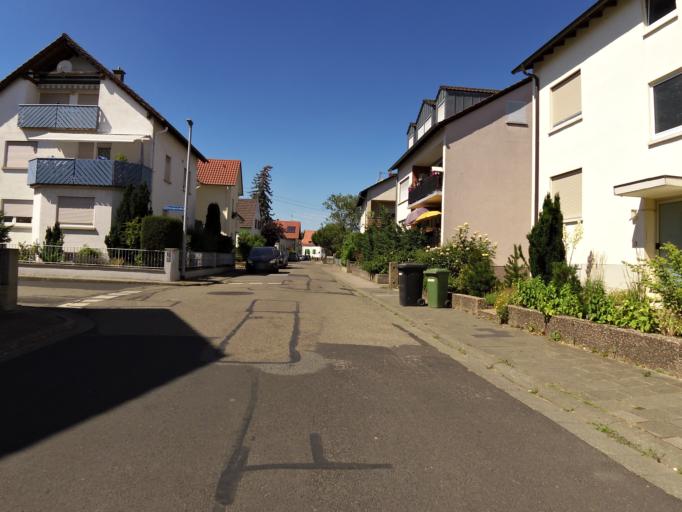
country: DE
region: Rheinland-Pfalz
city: Niederkirchen bei Deidesheim
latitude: 49.4109
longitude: 8.2114
